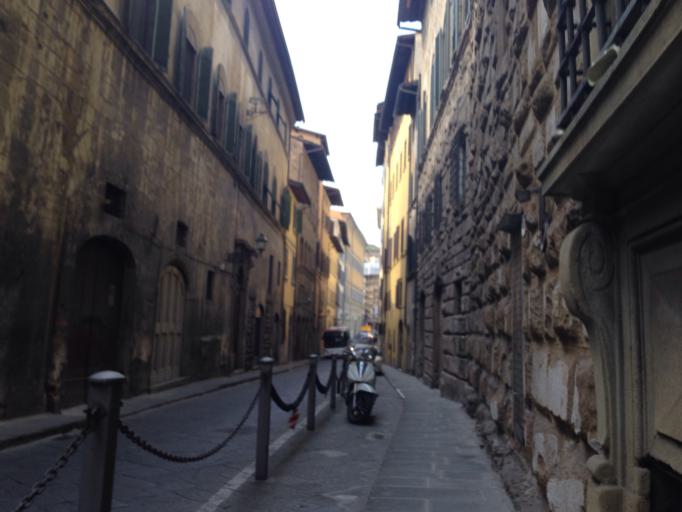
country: IT
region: Tuscany
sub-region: Province of Florence
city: Florence
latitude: 43.7661
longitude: 11.2559
